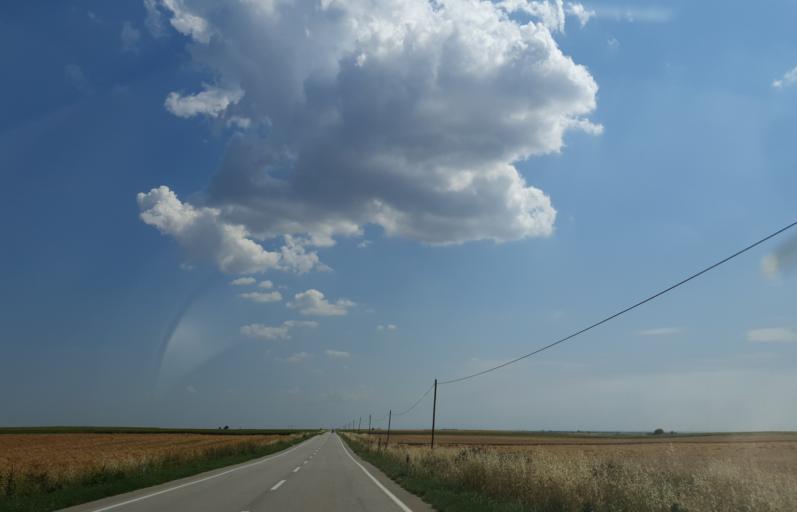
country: TR
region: Kirklareli
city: Buyukkaristiran
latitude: 41.4231
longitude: 27.5804
